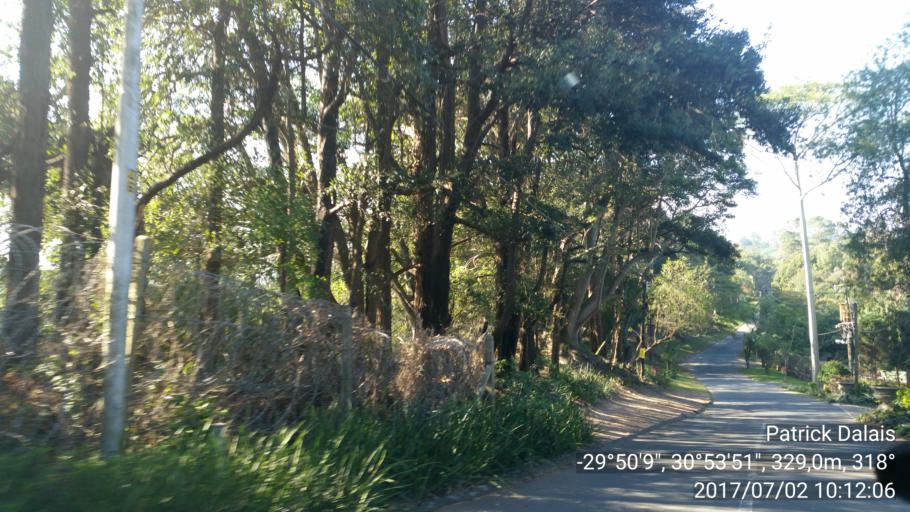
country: ZA
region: KwaZulu-Natal
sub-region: eThekwini Metropolitan Municipality
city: Berea
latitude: -29.8359
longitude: 30.8978
